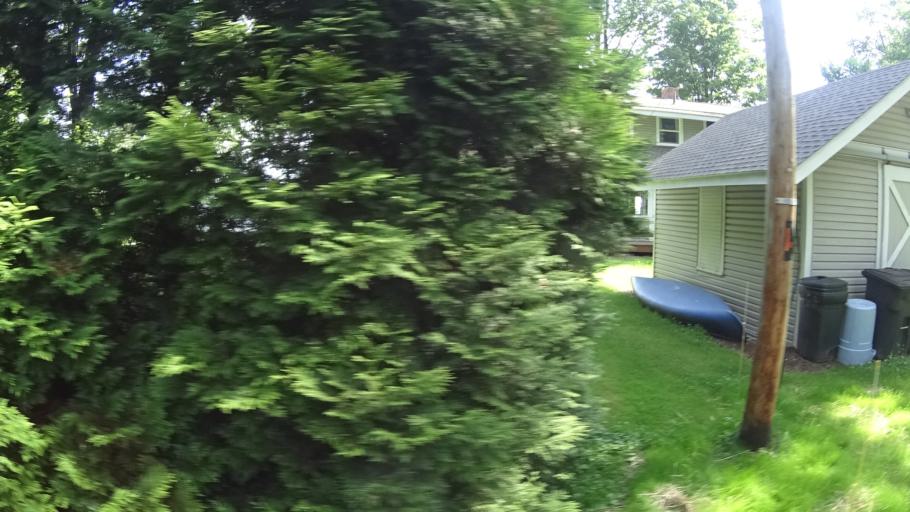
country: US
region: Ohio
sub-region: Erie County
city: Huron
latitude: 41.3830
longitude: -82.5098
